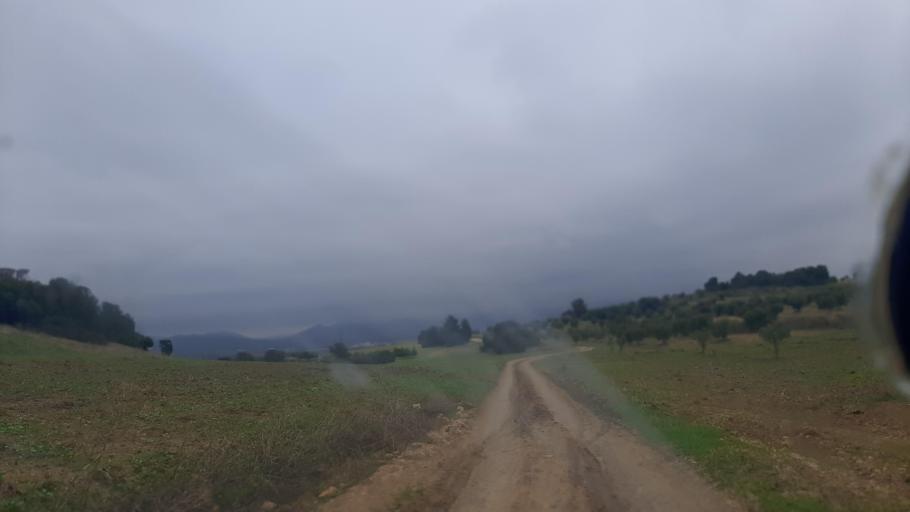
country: TN
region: Tunis
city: La Sebala du Mornag
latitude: 36.5767
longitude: 10.2914
